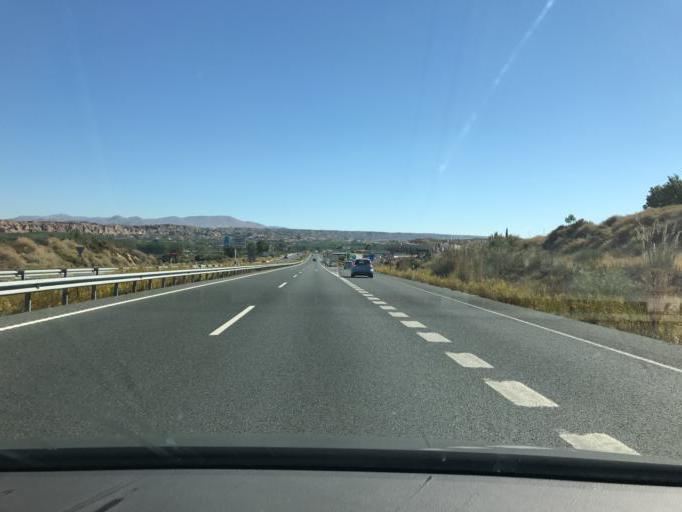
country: ES
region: Andalusia
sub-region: Provincia de Granada
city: Purullena
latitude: 37.3215
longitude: -3.1627
